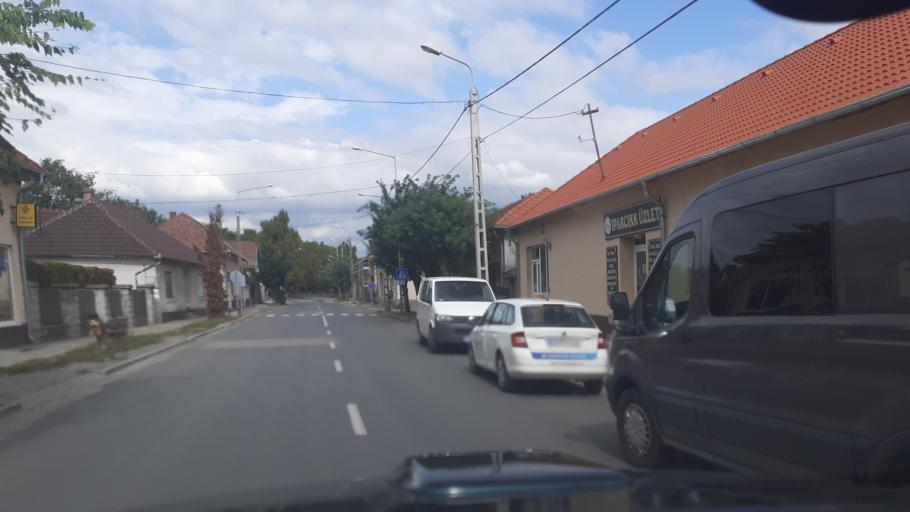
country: HU
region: Bacs-Kiskun
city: Dunavecse
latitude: 46.9152
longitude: 18.9714
